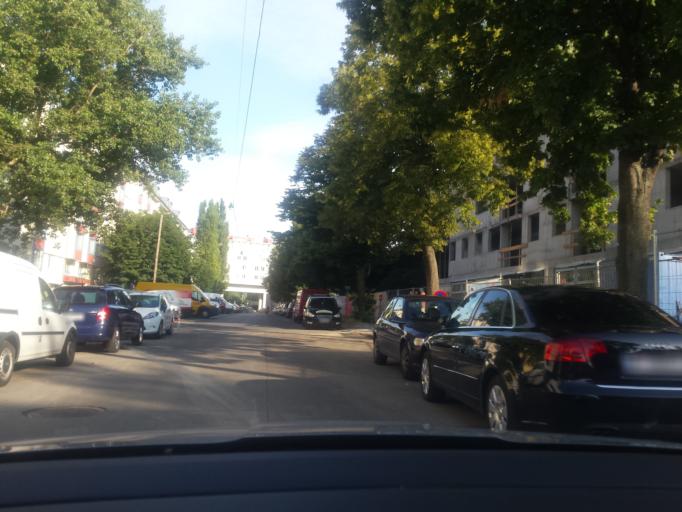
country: AT
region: Lower Austria
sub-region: Politischer Bezirk Wien-Umgebung
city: Schwechat
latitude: 48.1656
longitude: 16.4209
